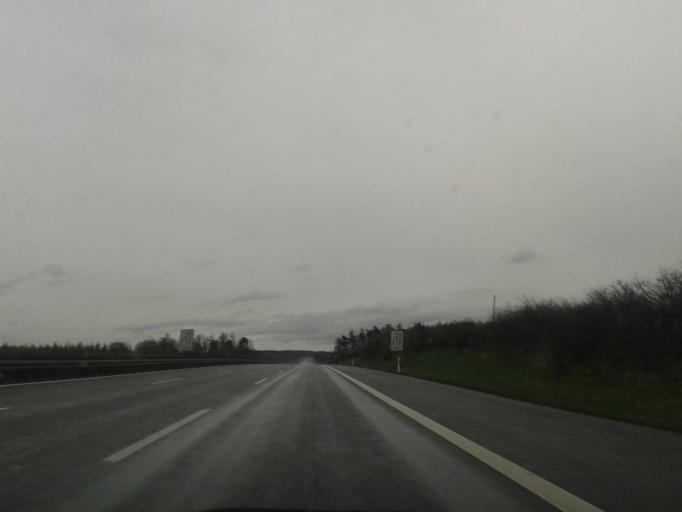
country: DE
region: Saxony
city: Wachau
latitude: 51.1715
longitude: 13.8737
